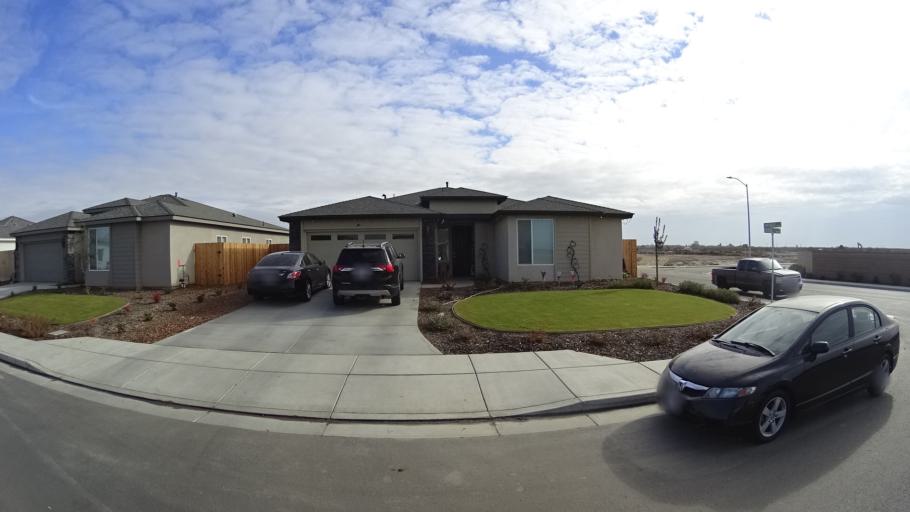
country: US
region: California
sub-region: Kern County
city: Rosedale
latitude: 35.3021
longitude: -119.1452
